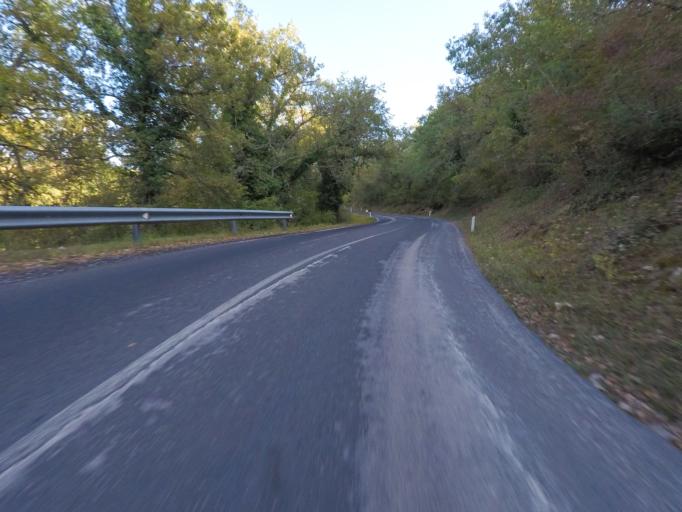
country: IT
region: Tuscany
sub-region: Provincia di Siena
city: Radda in Chianti
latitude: 43.4641
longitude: 11.3827
